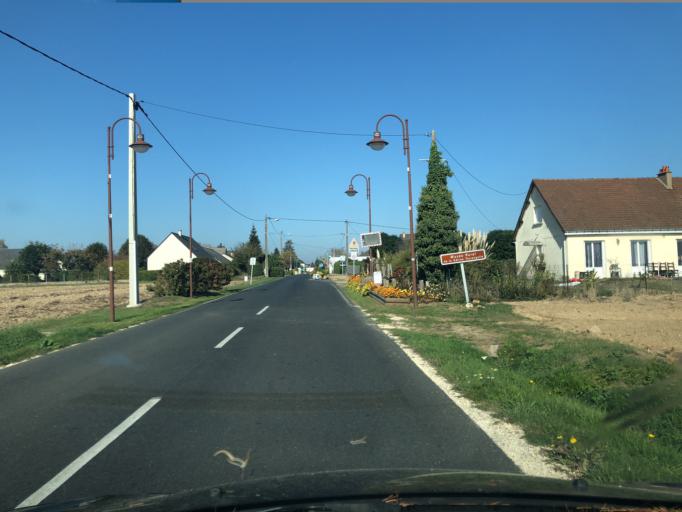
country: FR
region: Centre
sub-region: Departement d'Indre-et-Loire
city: Rouziers-de-Touraine
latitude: 47.5127
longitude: 0.6496
